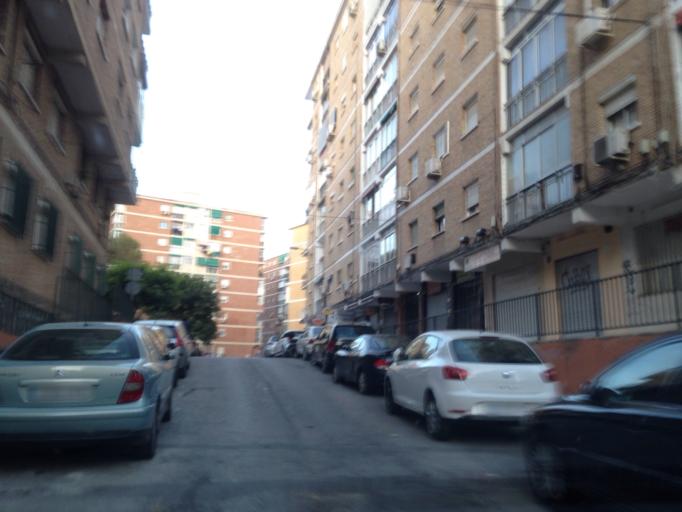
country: ES
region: Andalusia
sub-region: Provincia de Malaga
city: Malaga
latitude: 36.7303
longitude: -4.4409
